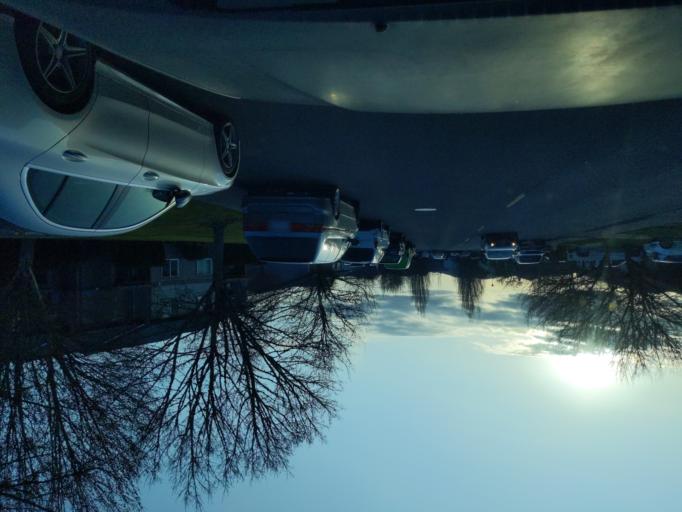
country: US
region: Oregon
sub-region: Yamhill County
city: McMinnville
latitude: 45.2018
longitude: -123.2184
